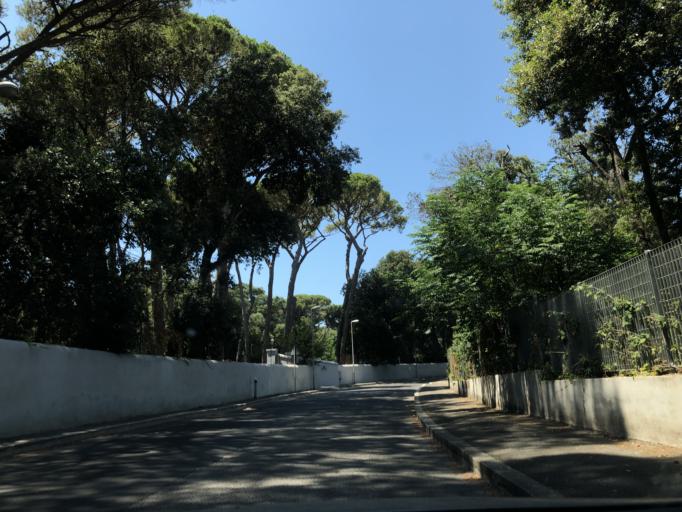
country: IT
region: Latium
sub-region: Citta metropolitana di Roma Capitale
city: Nettuno
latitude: 41.4572
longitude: 12.6458
